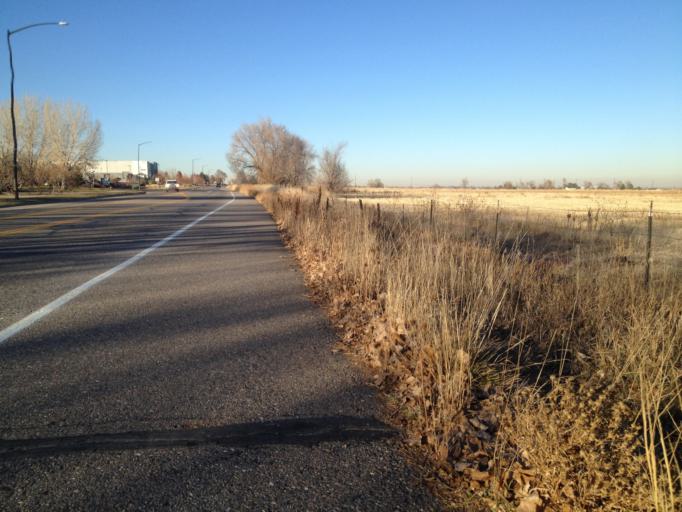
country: US
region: Colorado
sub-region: Boulder County
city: Louisville
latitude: 39.9661
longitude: -105.1093
